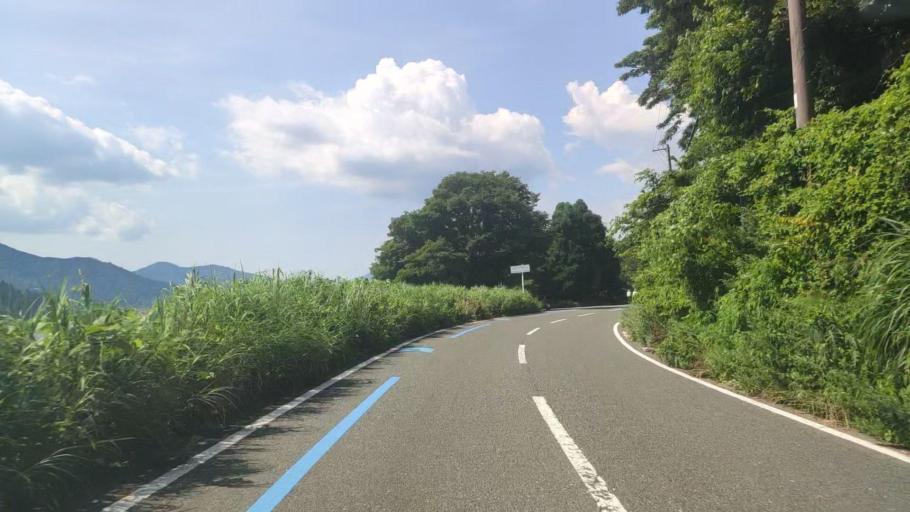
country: JP
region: Shiga Prefecture
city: Nagahama
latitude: 35.5048
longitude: 136.1692
